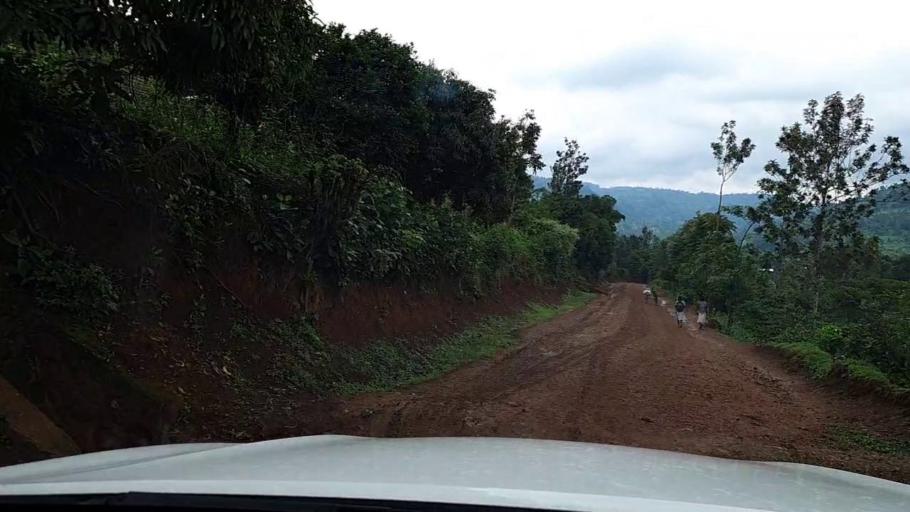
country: RW
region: Western Province
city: Cyangugu
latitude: -2.5697
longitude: 29.0328
